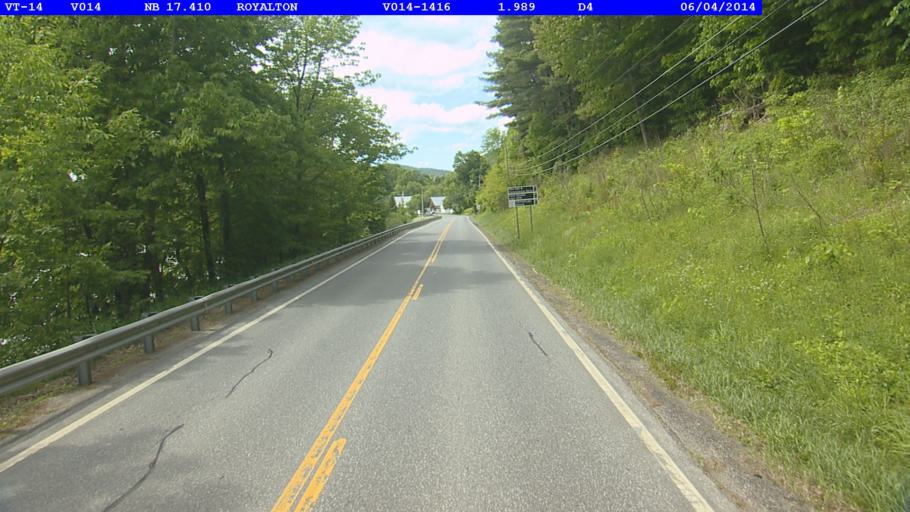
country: US
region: Vermont
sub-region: Orange County
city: Chelsea
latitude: 43.8204
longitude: -72.5135
